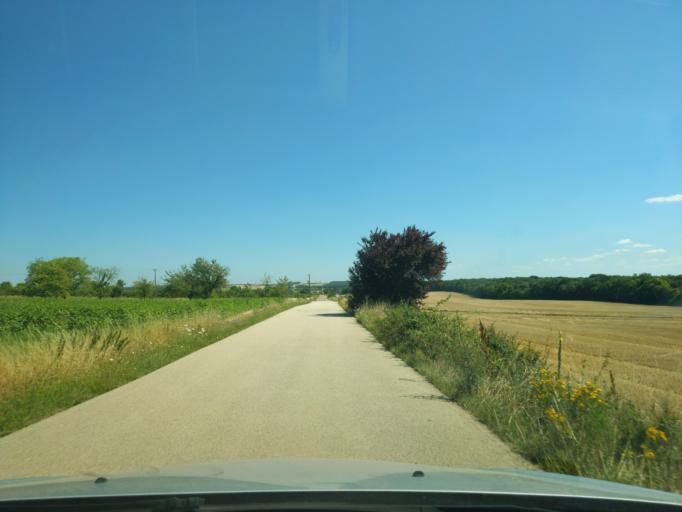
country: FR
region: Bourgogne
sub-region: Departement de la Cote-d'Or
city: Ruffey-les-Echirey
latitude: 47.3870
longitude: 5.0762
